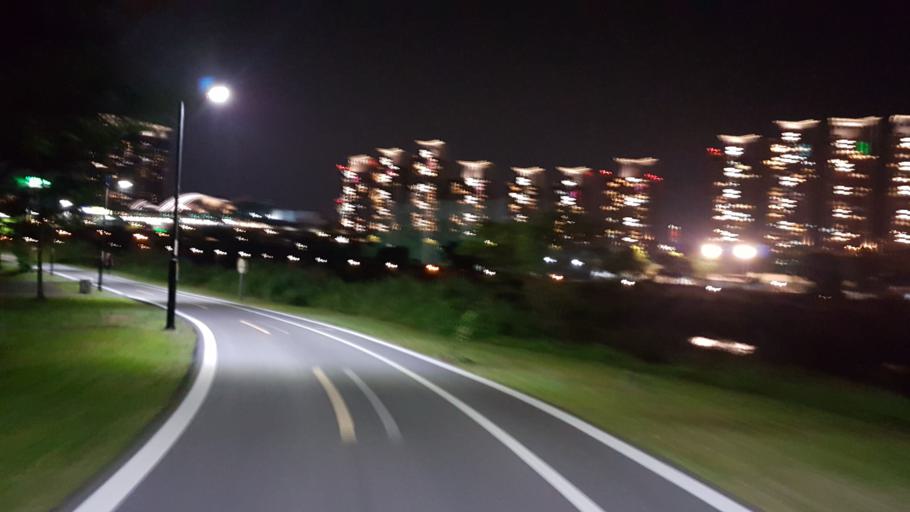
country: TW
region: Taipei
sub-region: Taipei
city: Banqiao
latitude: 24.9649
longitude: 121.5328
